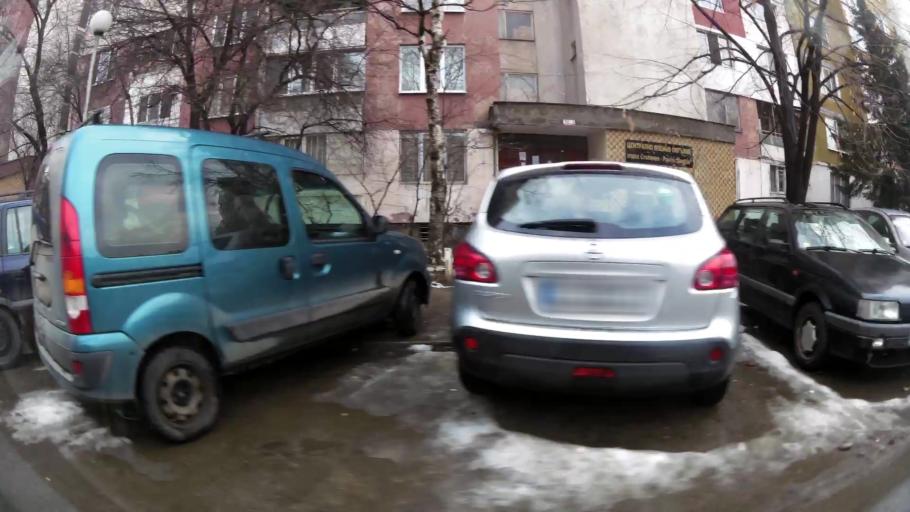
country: BG
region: Sofia-Capital
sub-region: Stolichna Obshtina
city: Sofia
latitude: 42.7117
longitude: 23.2666
